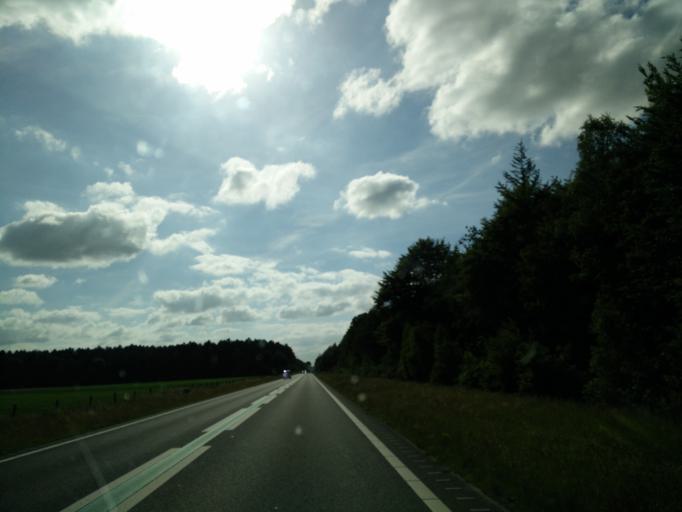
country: NL
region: Drenthe
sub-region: Gemeente Coevorden
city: Sleen
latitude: 52.7998
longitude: 6.7749
